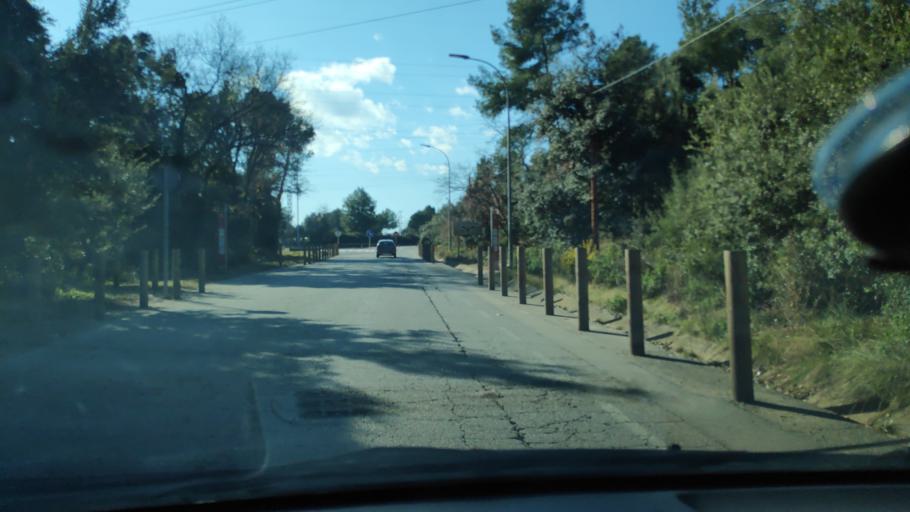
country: ES
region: Catalonia
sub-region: Provincia de Barcelona
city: Sant Quirze del Valles
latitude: 41.5549
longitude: 2.0552
